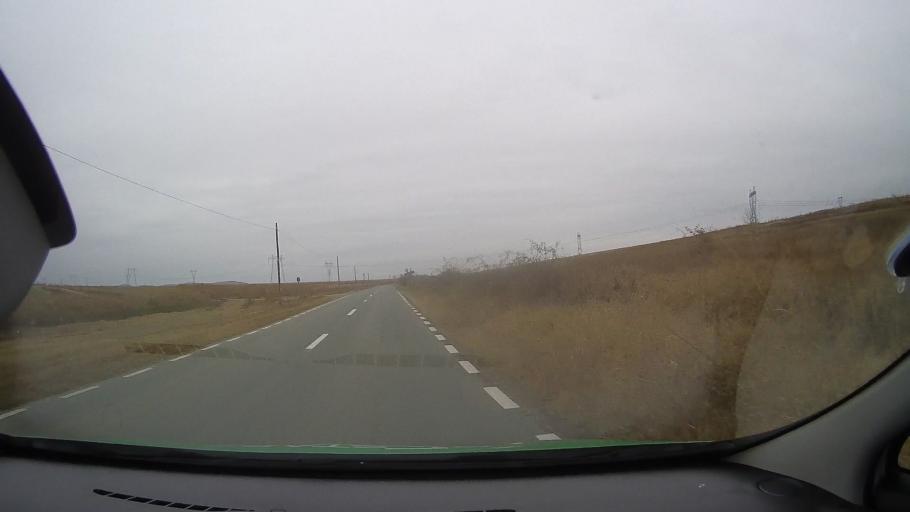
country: RO
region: Constanta
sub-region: Comuna Silistea
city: Silistea
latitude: 44.4326
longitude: 28.2188
